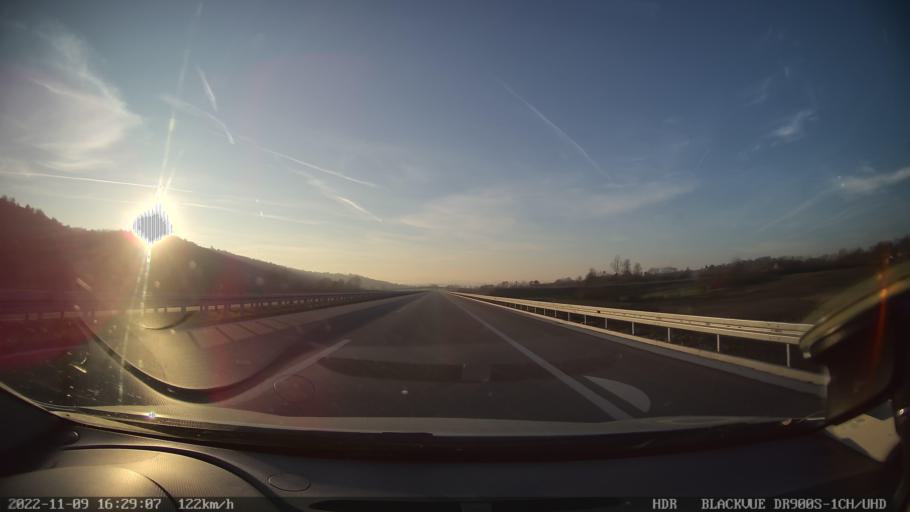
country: RS
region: Central Serbia
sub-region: Moravicki Okrug
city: Cacak
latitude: 43.9234
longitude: 20.3704
